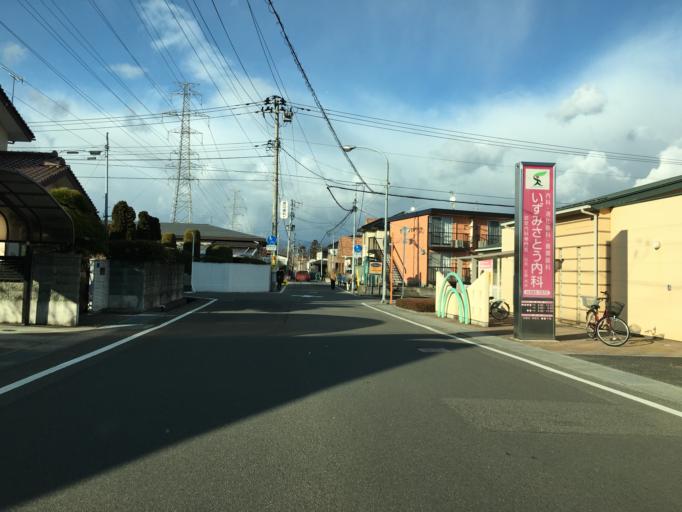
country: JP
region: Fukushima
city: Fukushima-shi
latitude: 37.7768
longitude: 140.4416
